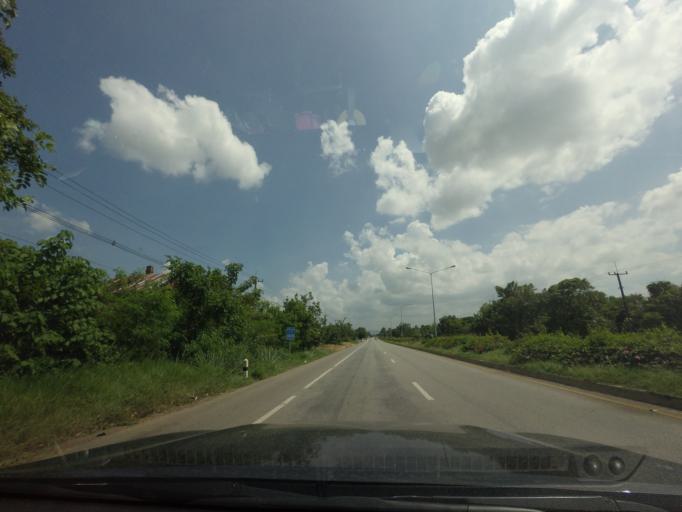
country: TH
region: Phetchabun
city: Phetchabun
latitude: 16.2581
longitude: 101.0571
